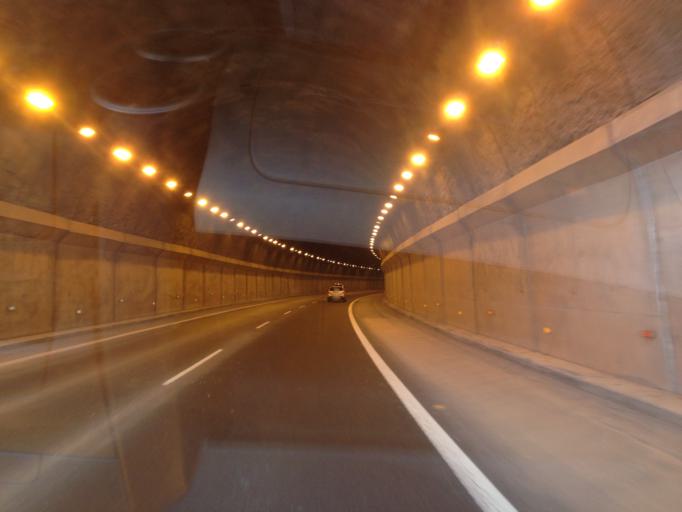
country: ES
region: Canary Islands
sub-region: Provincia de Las Palmas
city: Maspalomas
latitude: 27.7696
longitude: -15.6482
